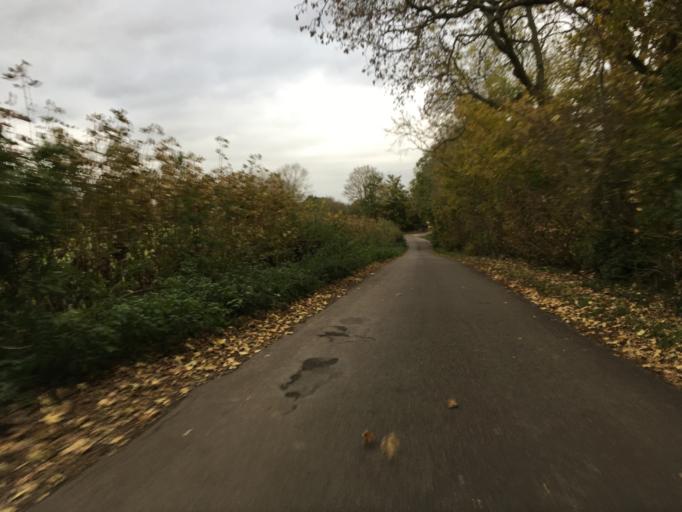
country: GB
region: England
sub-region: South Gloucestershire
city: Yate
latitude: 51.5448
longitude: -2.4542
